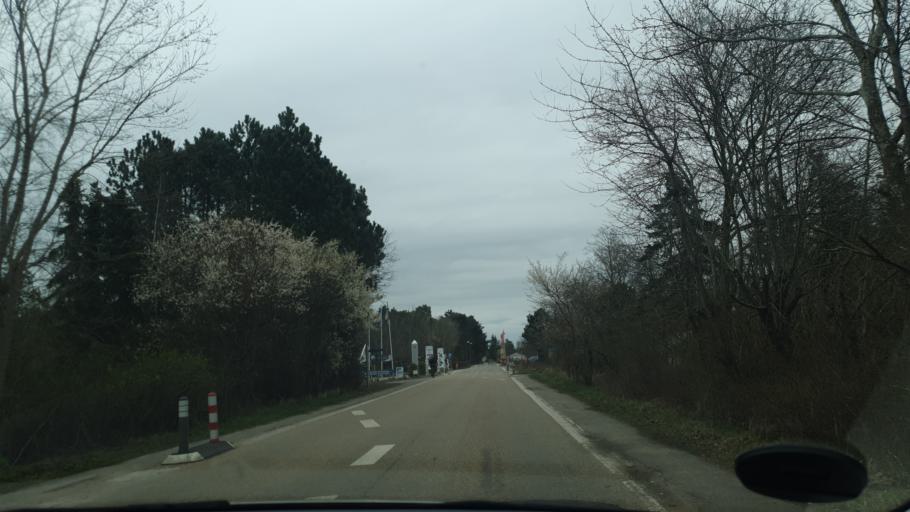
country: DK
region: Zealand
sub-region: Odsherred Kommune
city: Asnaes
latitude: 55.8572
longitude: 11.5248
